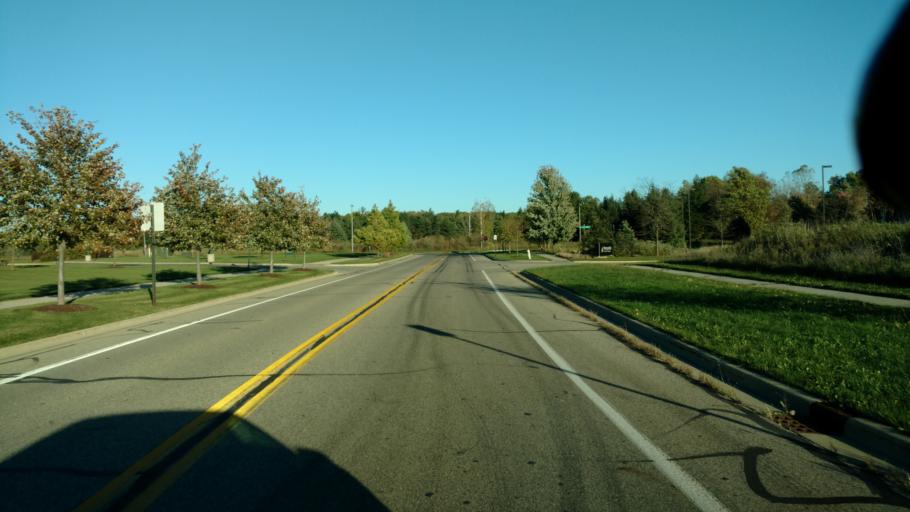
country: US
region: Michigan
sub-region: Ingham County
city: East Lansing
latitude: 42.7788
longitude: -84.5089
